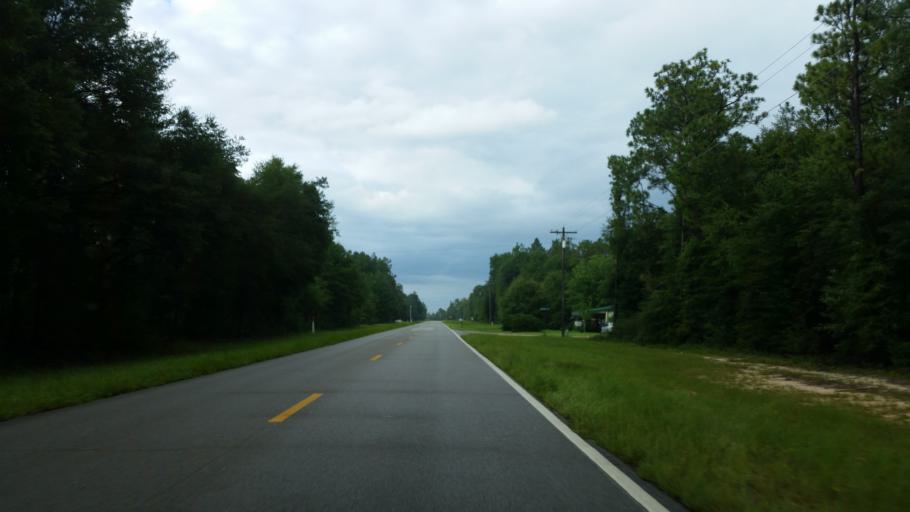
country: US
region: Florida
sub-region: Okaloosa County
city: Crestview
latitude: 30.6893
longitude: -86.7517
